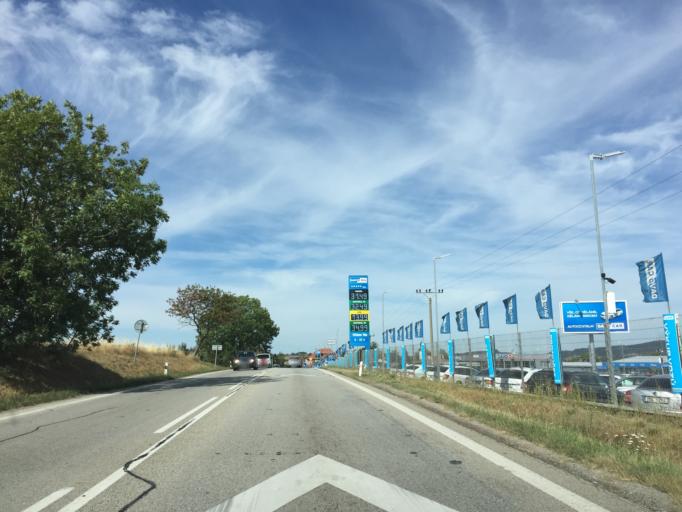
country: CZ
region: Central Bohemia
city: Votice
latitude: 49.6692
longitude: 14.6374
